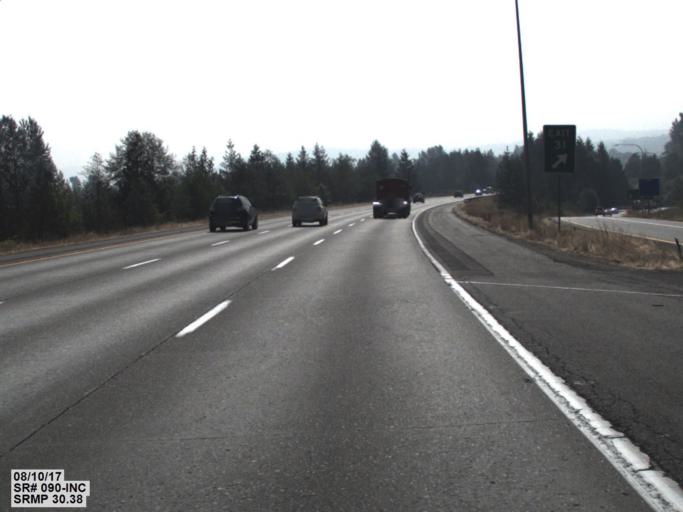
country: US
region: Washington
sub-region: King County
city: North Bend
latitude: 47.4902
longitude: -121.7996
